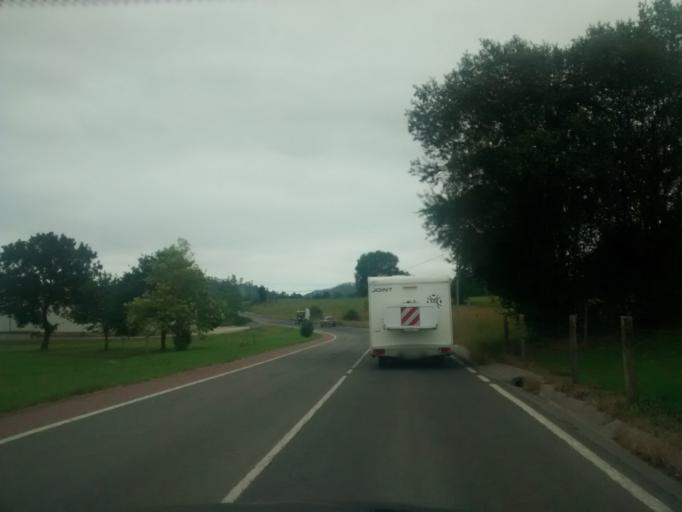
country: ES
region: Cantabria
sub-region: Provincia de Cantabria
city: Luzmela
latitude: 43.3088
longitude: -4.1975
